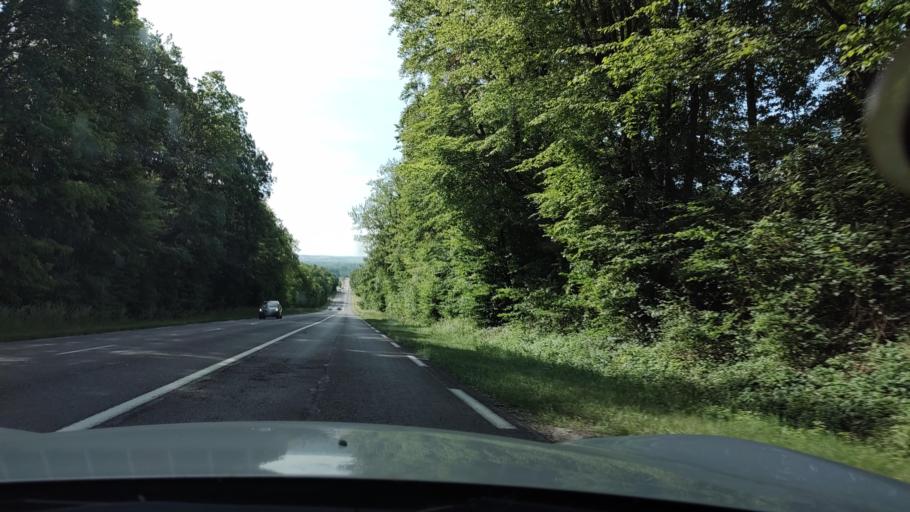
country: FR
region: Ile-de-France
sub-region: Departement de Seine-et-Marne
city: Sourdun
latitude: 48.5232
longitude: 3.4121
